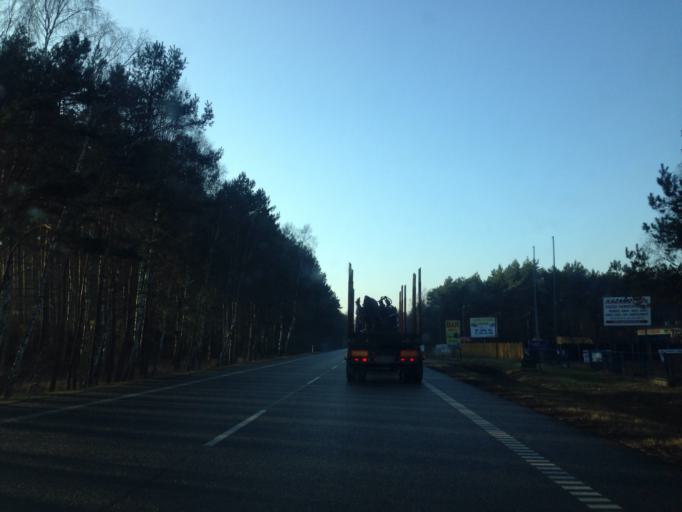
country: PL
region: Kujawsko-Pomorskie
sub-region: Powiat torunski
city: Zlawies Wielka
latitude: 53.0588
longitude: 18.2813
